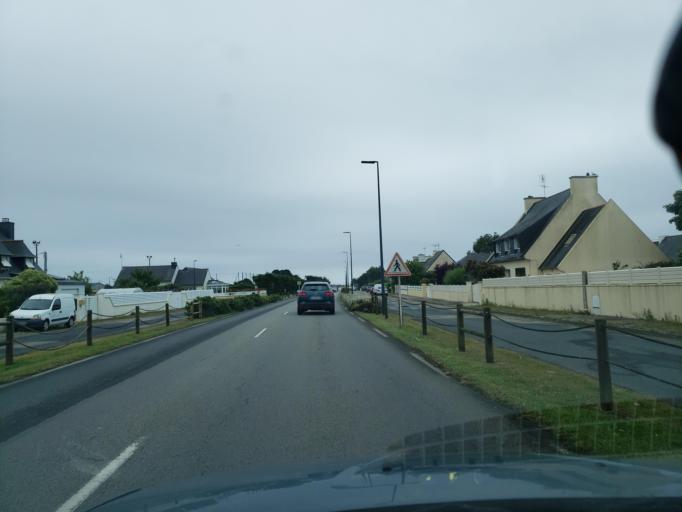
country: FR
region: Brittany
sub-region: Departement du Finistere
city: Guilvinec
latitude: 47.8068
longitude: -4.2798
